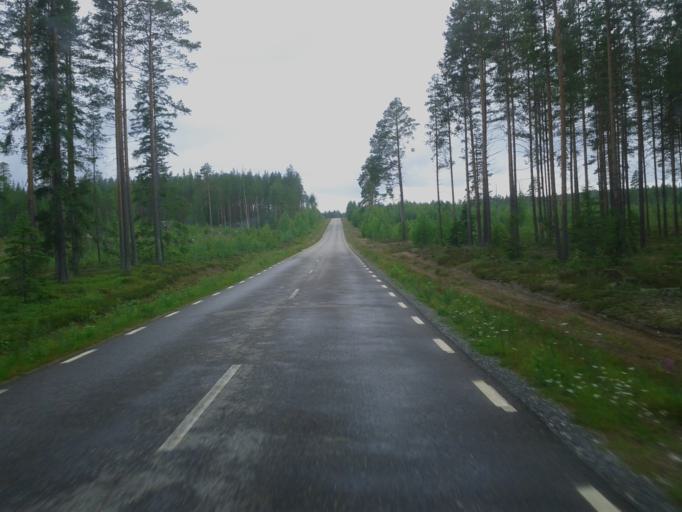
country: SE
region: Vaesterbotten
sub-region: Skelleftea Kommun
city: Kage
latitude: 64.9183
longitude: 20.9228
